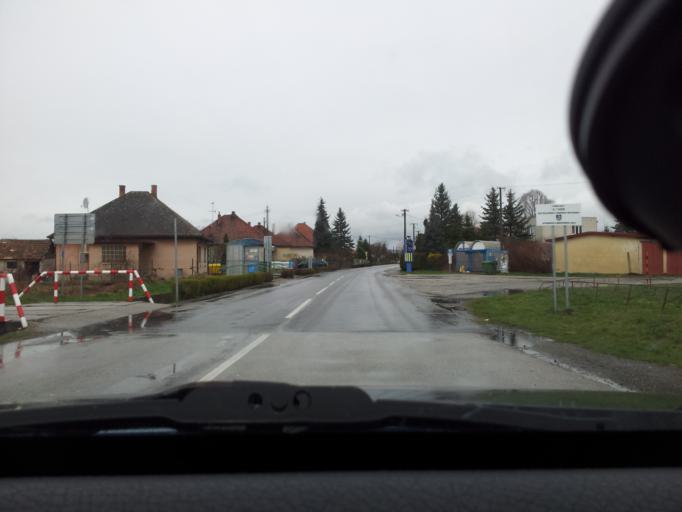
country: SK
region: Nitriansky
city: Tlmace
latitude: 48.3101
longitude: 18.5357
